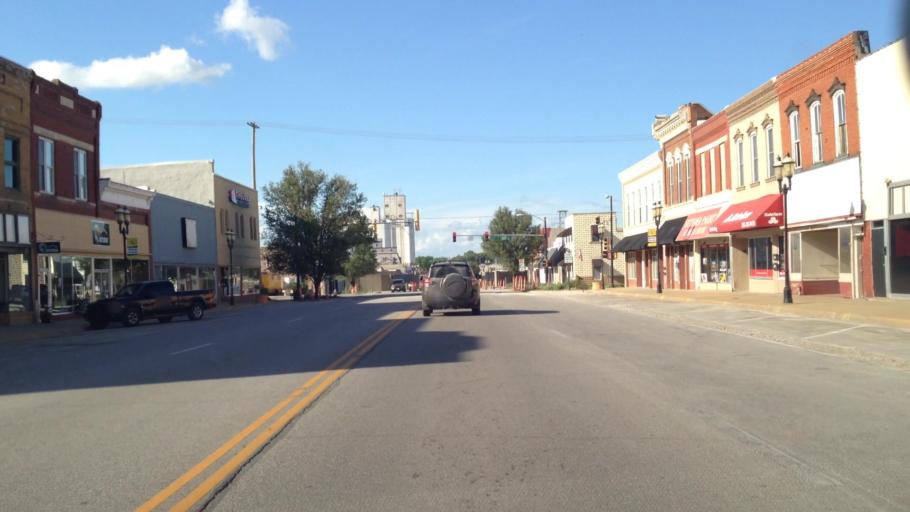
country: US
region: Kansas
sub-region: Franklin County
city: Ottawa
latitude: 38.6163
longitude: -95.2685
